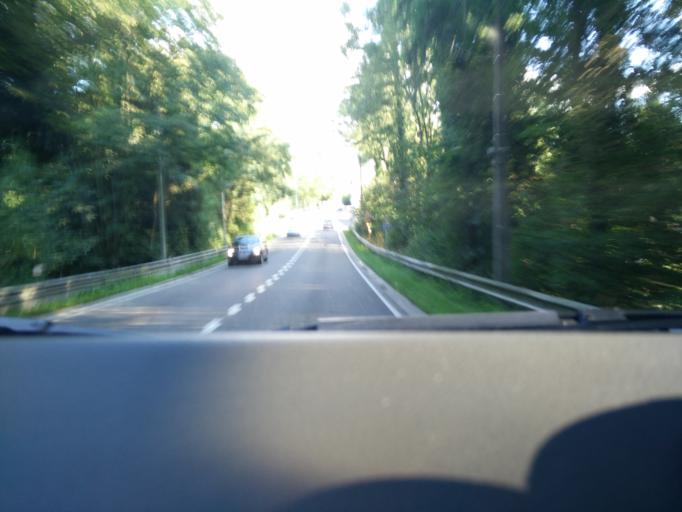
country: BE
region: Wallonia
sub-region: Province du Hainaut
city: Beaumont
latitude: 50.2402
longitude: 4.2365
